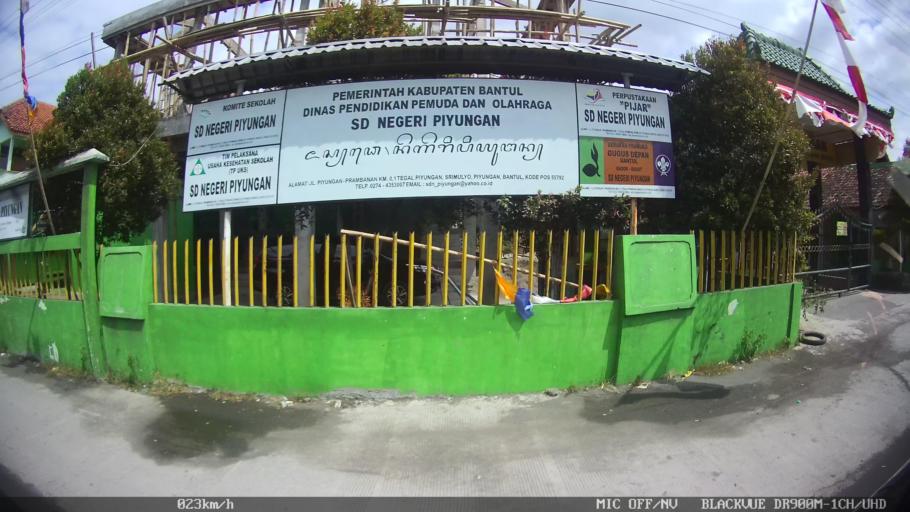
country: ID
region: Daerah Istimewa Yogyakarta
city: Depok
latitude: -7.8371
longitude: 110.4764
